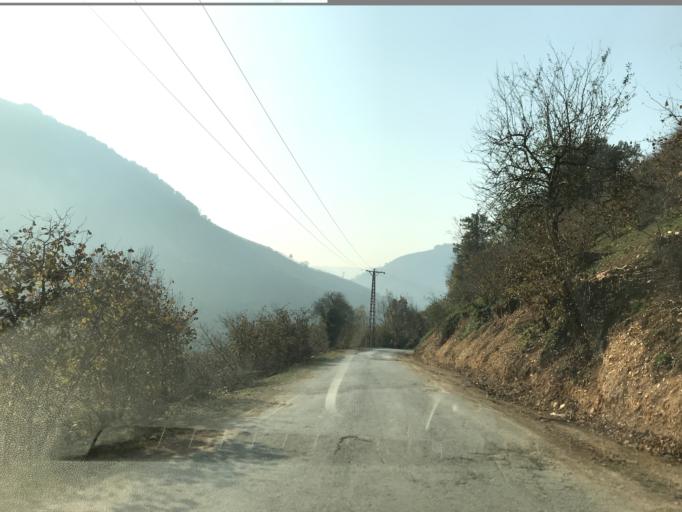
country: TR
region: Duzce
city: Cumayeri
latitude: 40.9392
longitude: 30.9322
